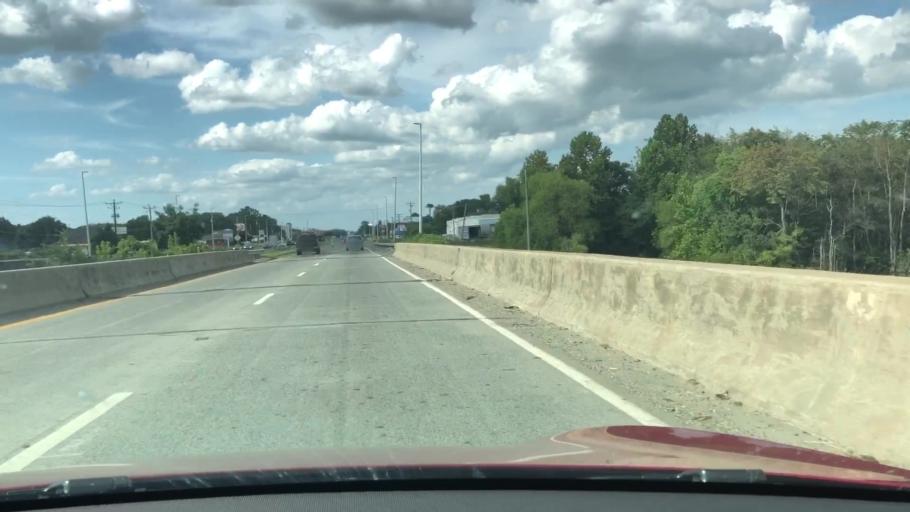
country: US
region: Delaware
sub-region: Sussex County
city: Seaford
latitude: 38.6434
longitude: -75.5935
